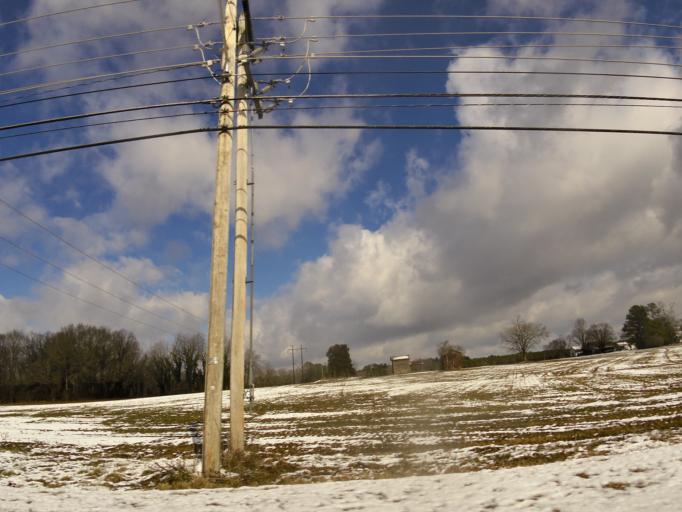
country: US
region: North Carolina
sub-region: Wilson County
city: Wilson
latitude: 35.7206
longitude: -77.9600
